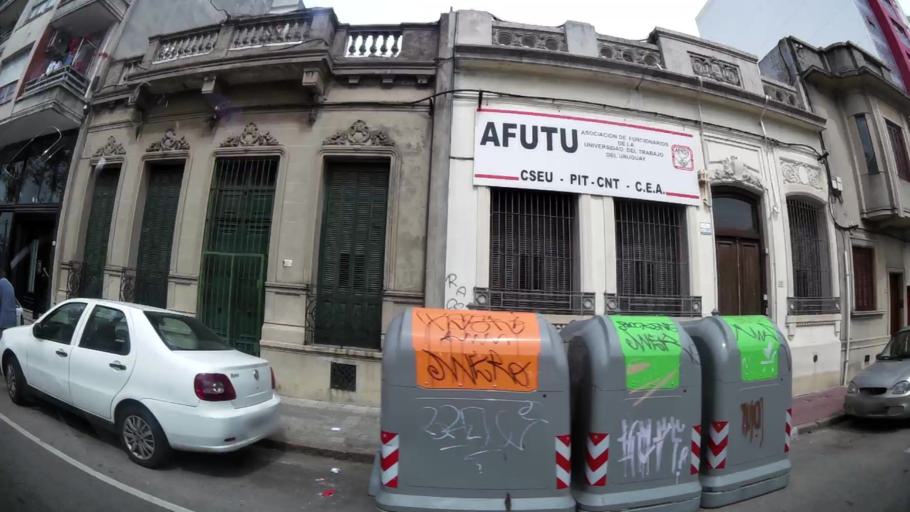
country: UY
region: Montevideo
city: Montevideo
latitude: -34.9084
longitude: -56.1783
